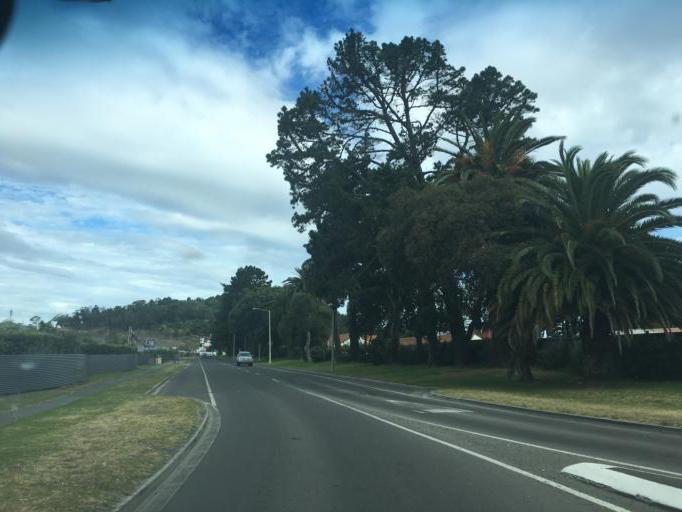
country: NZ
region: Gisborne
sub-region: Gisborne District
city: Gisborne
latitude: -38.6697
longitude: 178.0182
